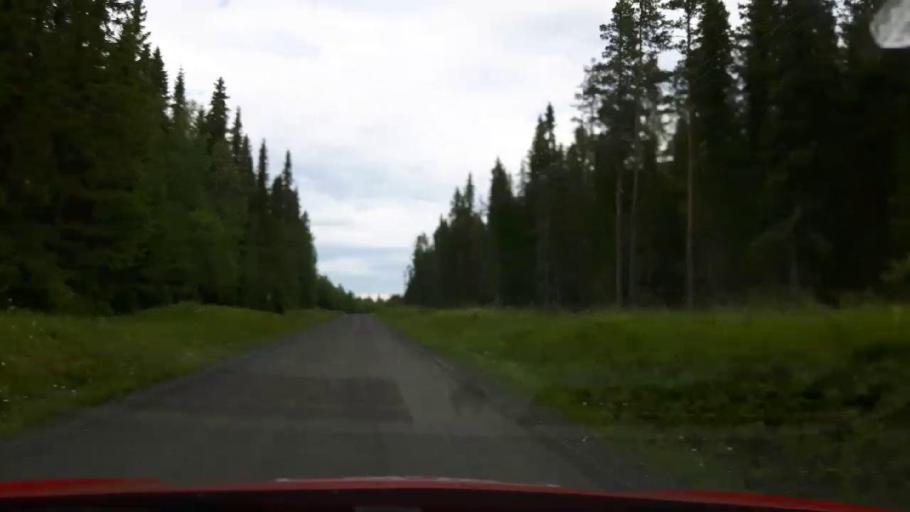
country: SE
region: Jaemtland
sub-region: Stroemsunds Kommun
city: Stroemsund
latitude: 63.4672
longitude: 15.2858
